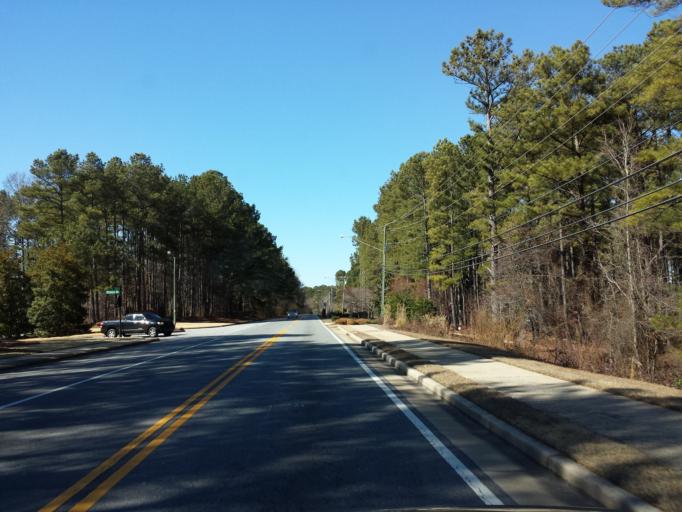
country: US
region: Georgia
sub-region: Cobb County
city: Fair Oaks
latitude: 33.9103
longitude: -84.6079
